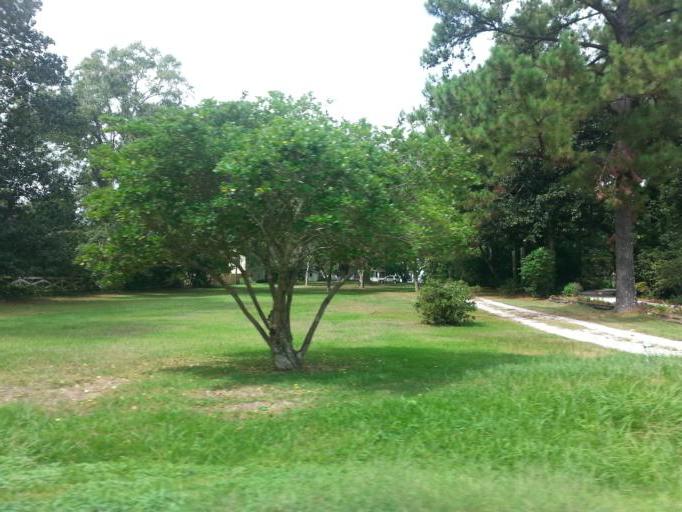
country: US
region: Alabama
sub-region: Baldwin County
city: Fairhope
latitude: 30.5089
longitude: -87.9193
